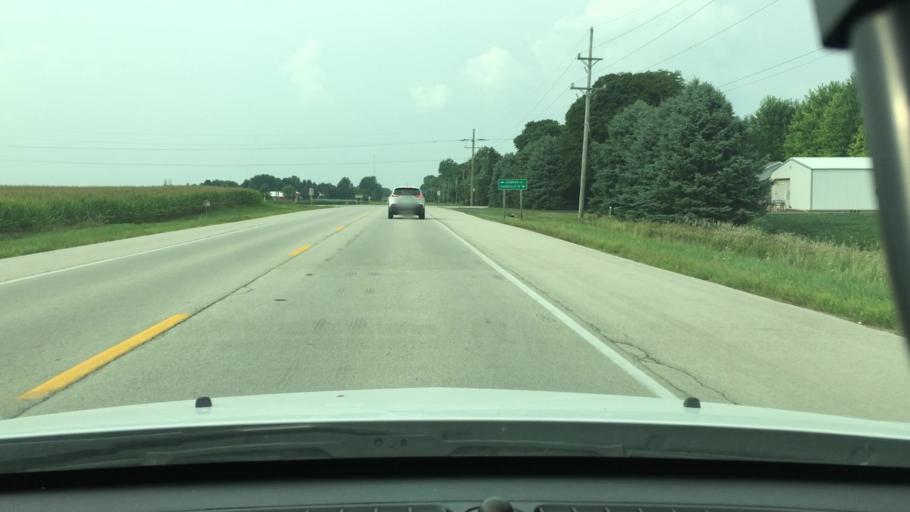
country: US
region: Illinois
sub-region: DeKalb County
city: Waterman
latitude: 41.8478
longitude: -88.7538
